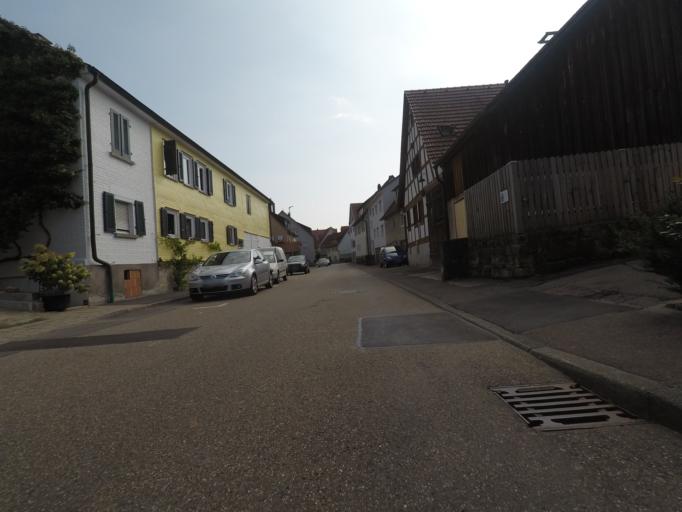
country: DE
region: Baden-Wuerttemberg
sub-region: Regierungsbezirk Stuttgart
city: Winterbach
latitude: 48.7994
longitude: 9.4767
